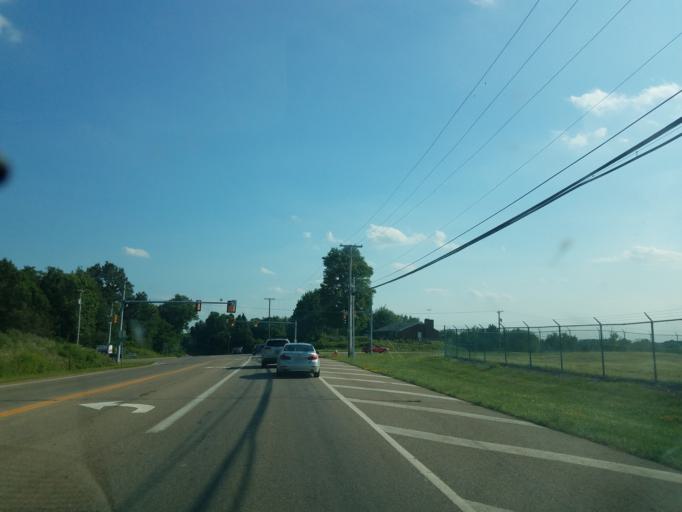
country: US
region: Ohio
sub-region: Summit County
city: Greensburg
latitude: 40.9005
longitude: -81.4399
